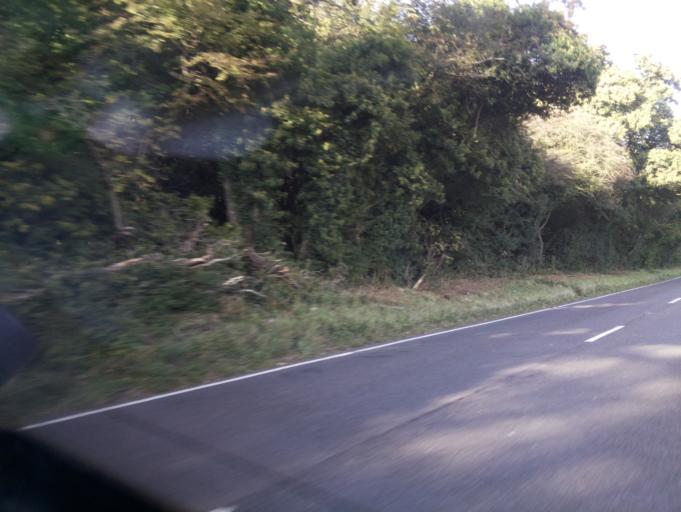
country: GB
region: England
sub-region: Hampshire
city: Four Marks
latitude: 51.0561
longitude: -1.0372
